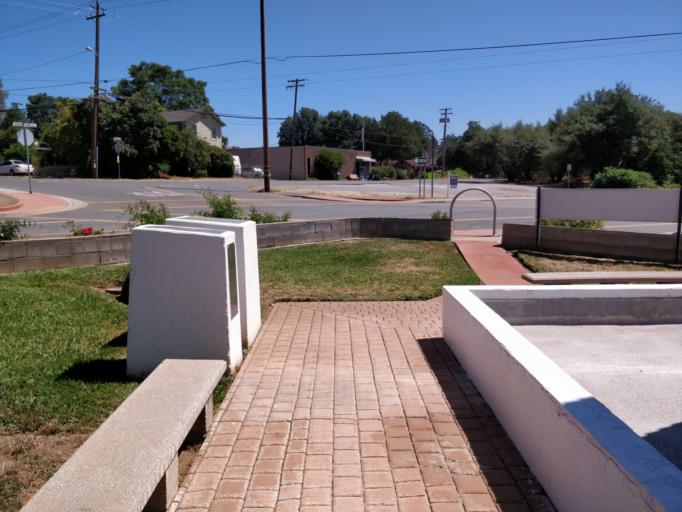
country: US
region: California
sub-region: Shasta County
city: Shasta Lake
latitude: 40.6807
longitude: -122.3674
